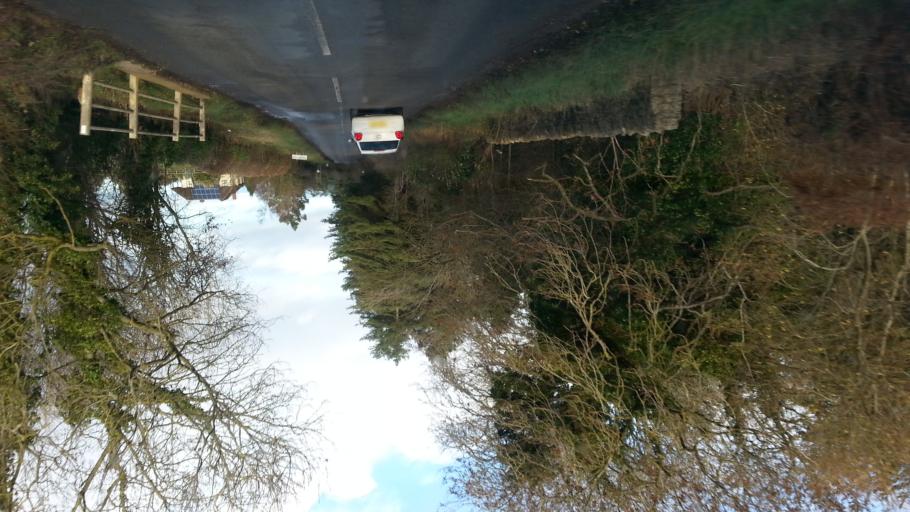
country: GB
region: England
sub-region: Oxfordshire
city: Stanford in the Vale
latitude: 51.6548
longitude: -1.5009
